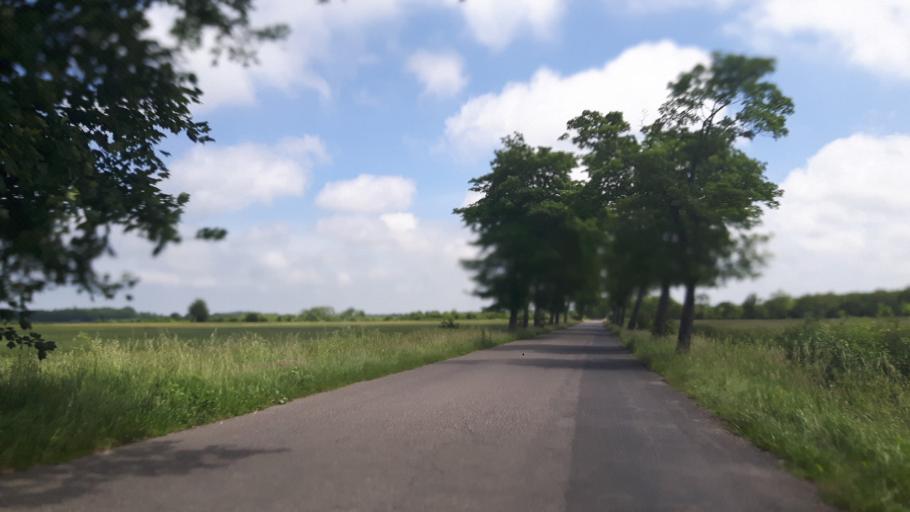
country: PL
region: West Pomeranian Voivodeship
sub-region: Powiat slawienski
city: Slawno
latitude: 54.5086
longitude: 16.6018
